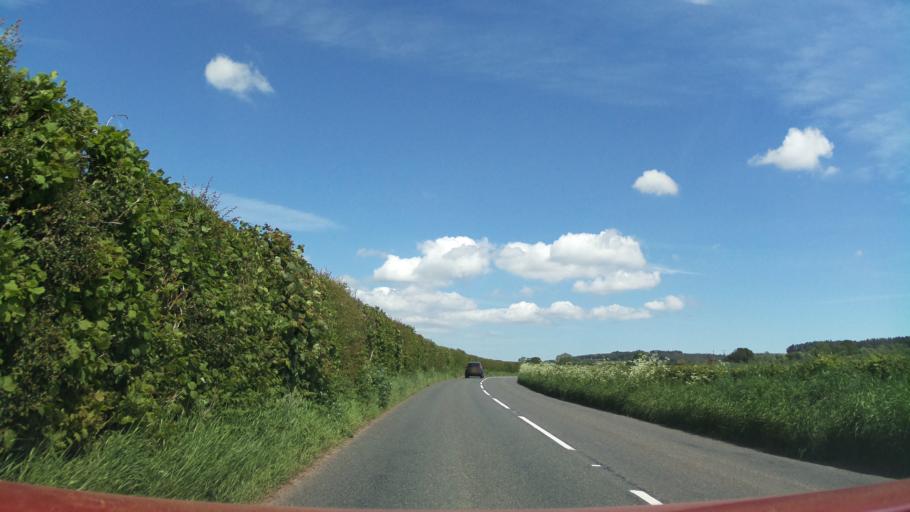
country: GB
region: Wales
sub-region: Monmouthshire
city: Mitchel Troy
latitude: 51.7334
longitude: -2.7455
